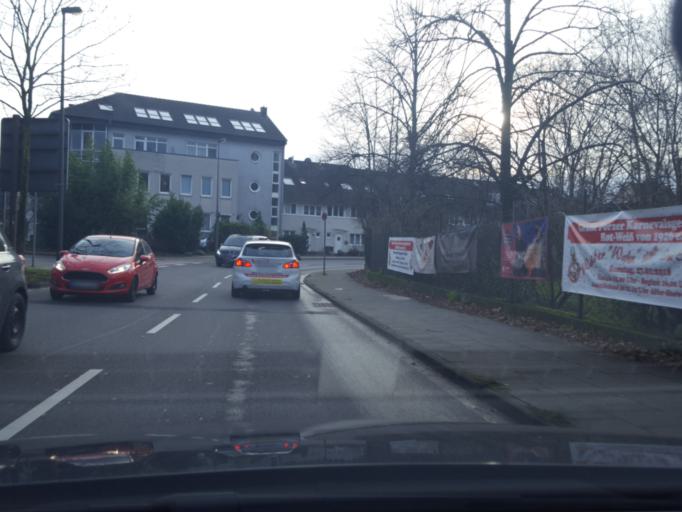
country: DE
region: North Rhine-Westphalia
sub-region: Regierungsbezirk Koln
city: Wahn-Heide
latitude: 50.8569
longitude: 7.0853
